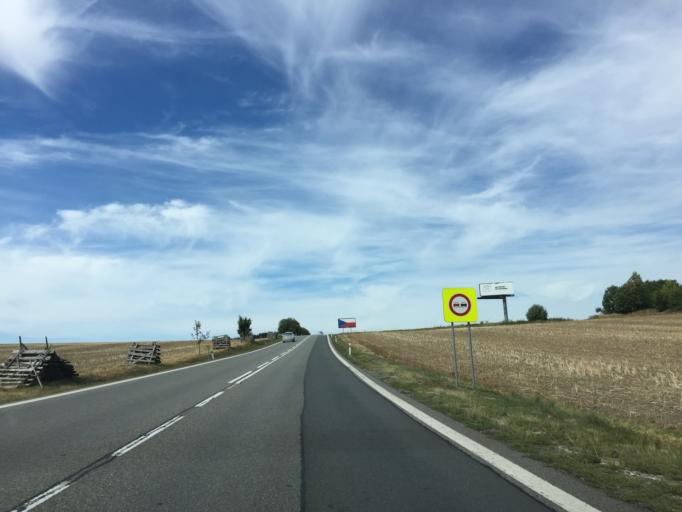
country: CZ
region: Jihocesky
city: Chotoviny
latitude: 49.5601
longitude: 14.6624
